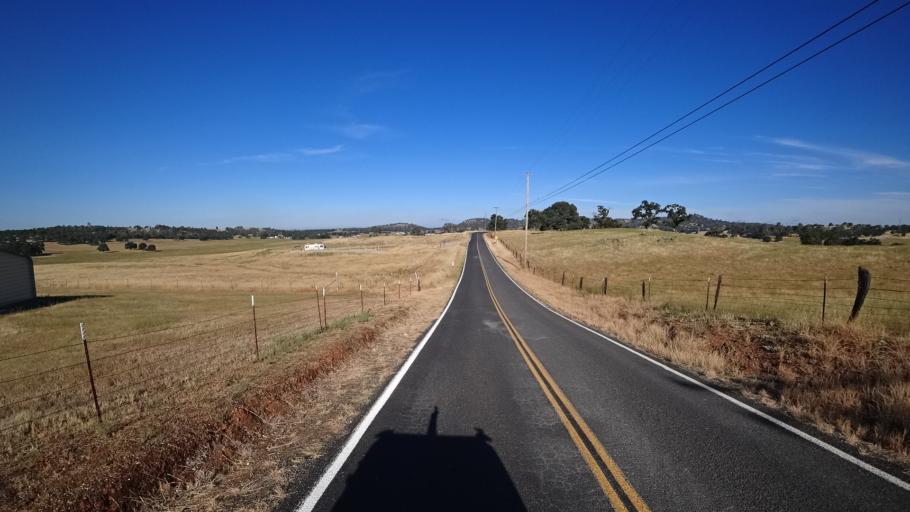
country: US
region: California
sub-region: Calaveras County
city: Valley Springs
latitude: 38.1892
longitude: -120.8036
